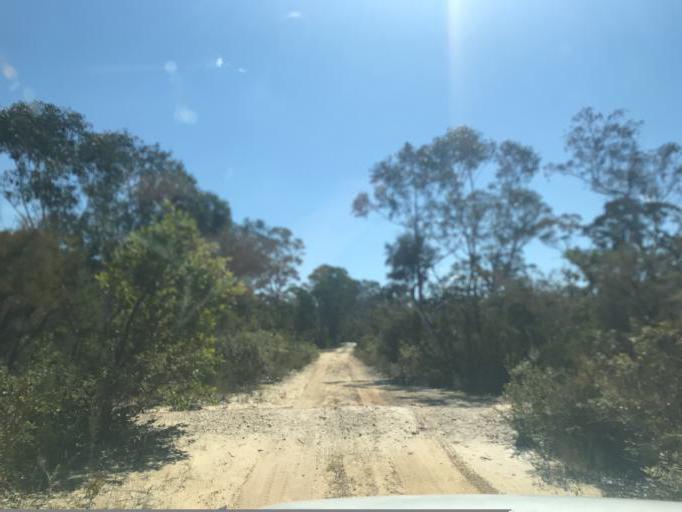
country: AU
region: New South Wales
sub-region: Wyong Shire
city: Little Jilliby
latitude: -33.1560
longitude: 151.0993
